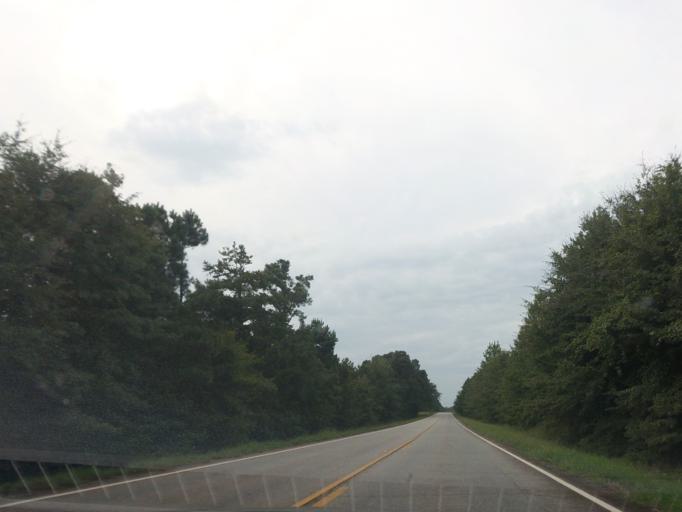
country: US
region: Georgia
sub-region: Twiggs County
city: Jeffersonville
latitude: 32.7005
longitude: -83.3772
